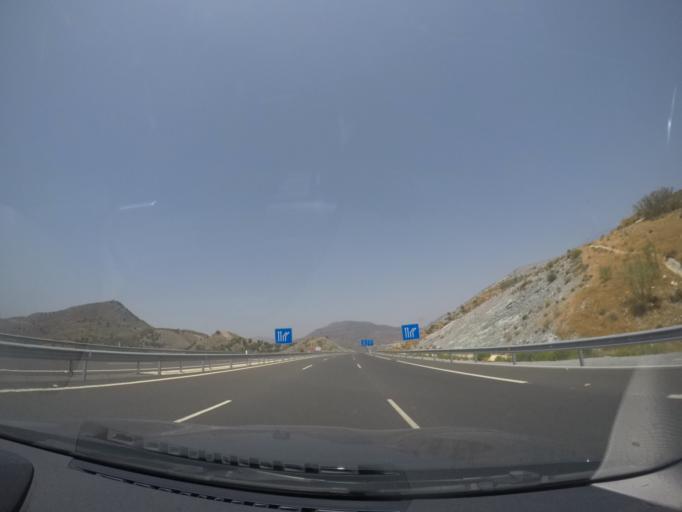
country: ES
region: Andalusia
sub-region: Provincia de Granada
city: Motril
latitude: 36.7784
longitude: -3.5008
